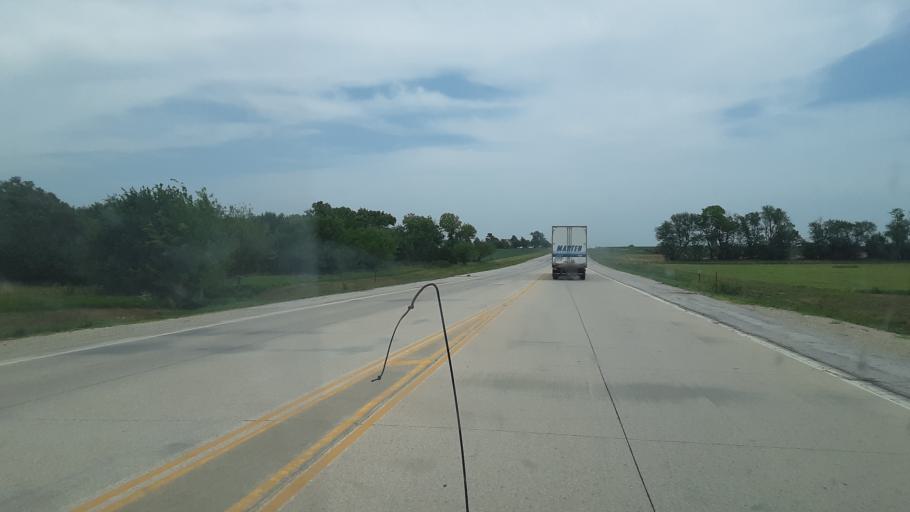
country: US
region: Kansas
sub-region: Allen County
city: Iola
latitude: 37.9220
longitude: -95.2920
